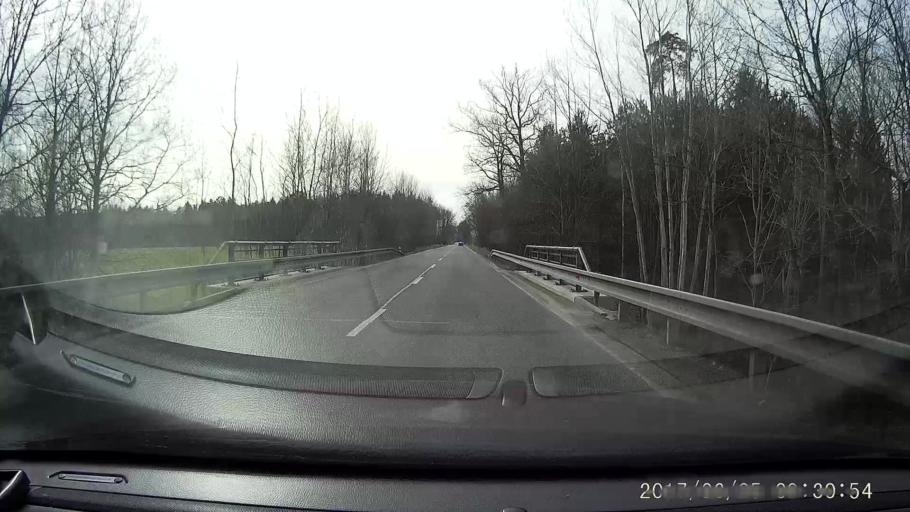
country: PL
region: Silesian Voivodeship
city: Zawidow
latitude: 50.9972
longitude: 15.0741
